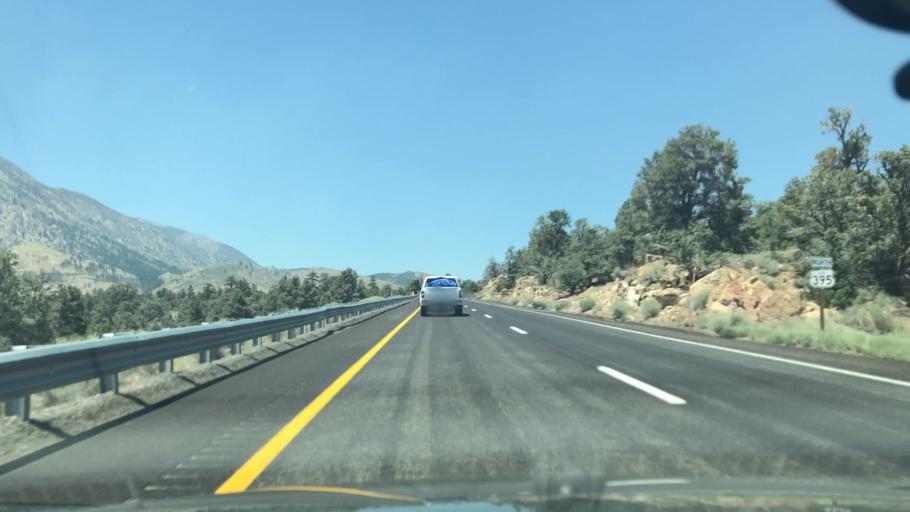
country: US
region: California
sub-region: Inyo County
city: West Bishop
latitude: 37.5223
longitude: -118.6158
